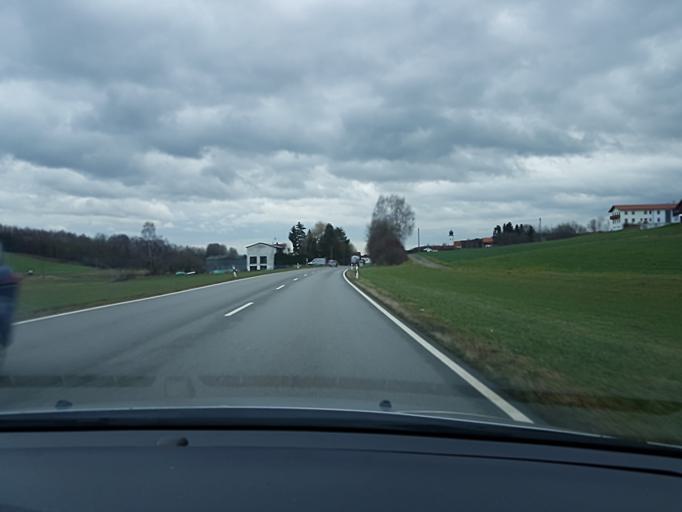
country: DE
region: Bavaria
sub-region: Upper Bavaria
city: Egglkofen
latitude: 48.3778
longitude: 12.4734
